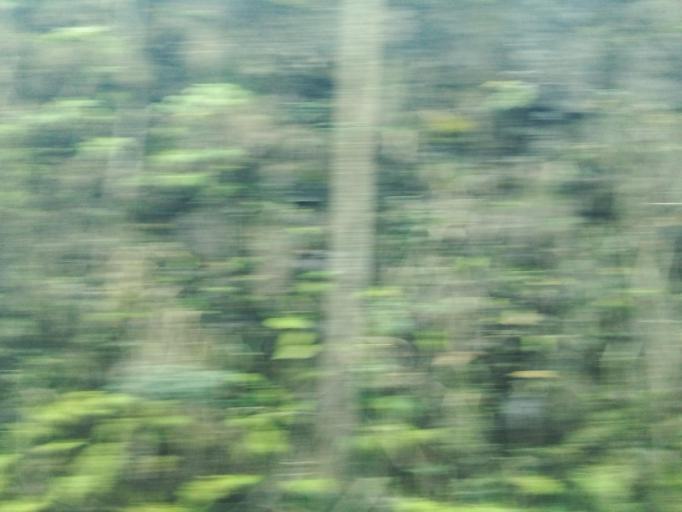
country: BR
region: Minas Gerais
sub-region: Rio Piracicaba
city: Rio Piracicaba
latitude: -19.8923
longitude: -43.1420
